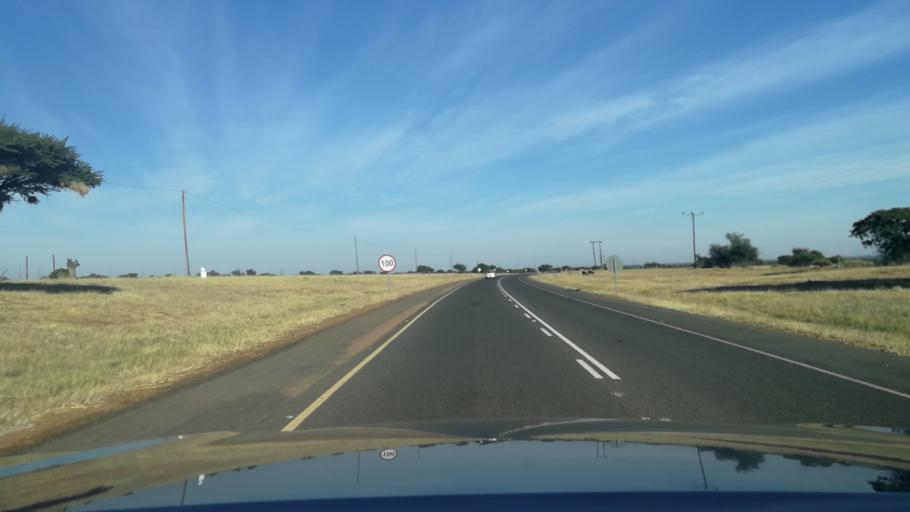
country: BW
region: South East
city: Janeng
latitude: -25.4779
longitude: 25.5133
